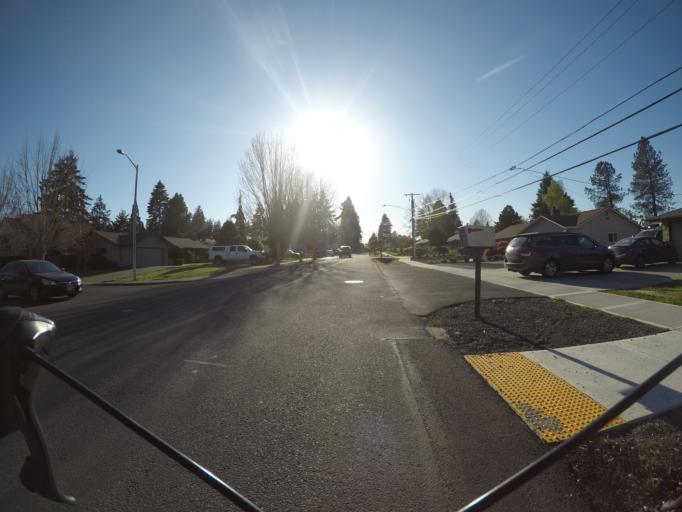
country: US
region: Oregon
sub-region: Washington County
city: Aloha
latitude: 45.4788
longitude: -122.8712
